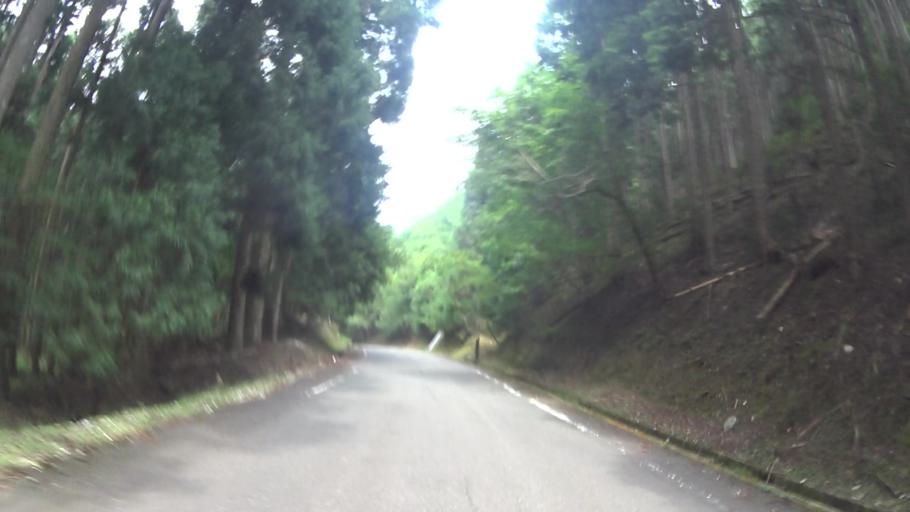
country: JP
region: Kyoto
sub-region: Kyoto-shi
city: Kamigyo-ku
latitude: 35.2039
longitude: 135.6656
